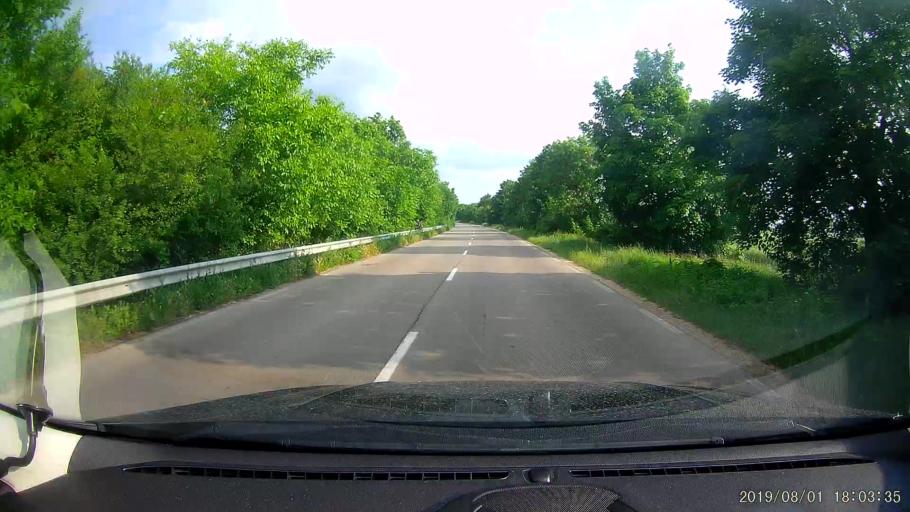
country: BG
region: Silistra
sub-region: Obshtina Alfatar
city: Alfatar
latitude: 43.9243
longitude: 27.2888
